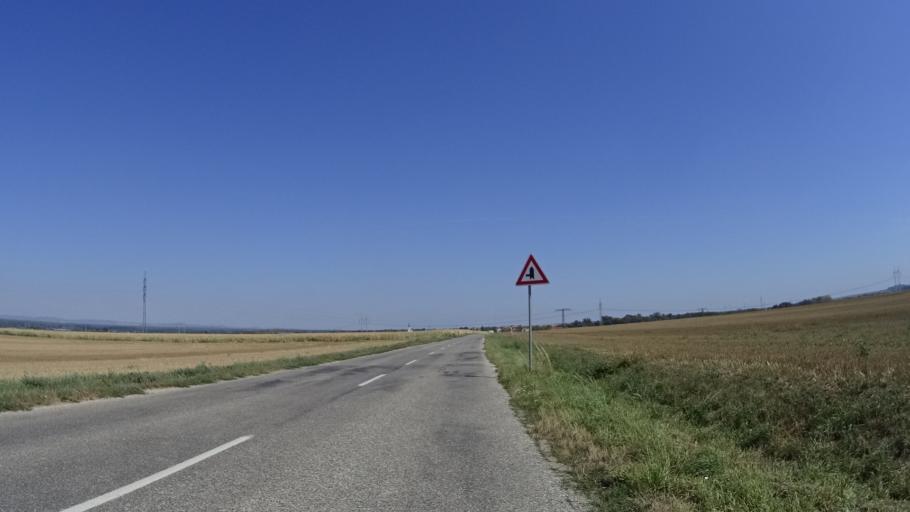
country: CZ
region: South Moravian
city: Sudomerice
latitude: 48.8566
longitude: 17.2441
